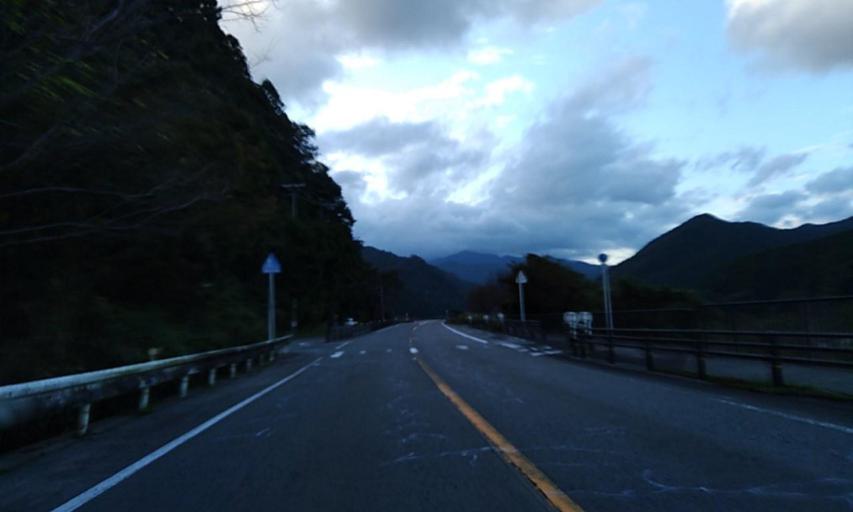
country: JP
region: Wakayama
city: Shingu
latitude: 33.7238
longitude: 135.9627
